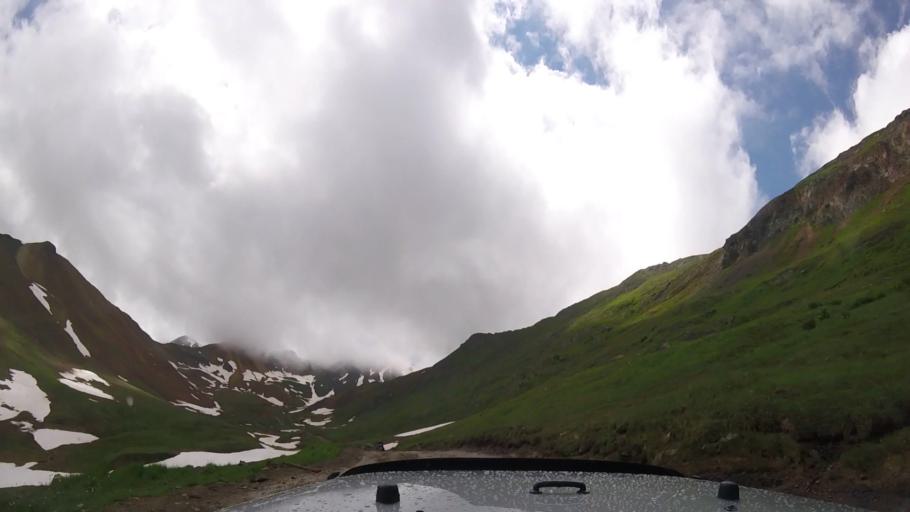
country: US
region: Colorado
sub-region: Ouray County
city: Ouray
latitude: 37.9243
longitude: -107.6108
